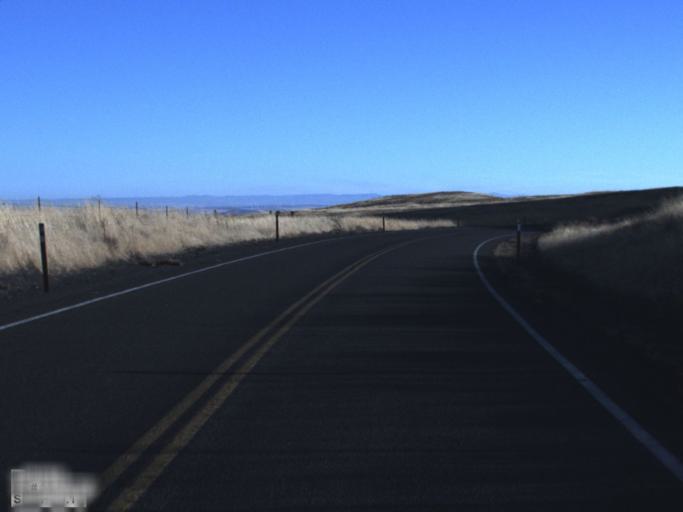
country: US
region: Washington
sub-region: Walla Walla County
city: Waitsburg
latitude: 46.6409
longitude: -118.2446
